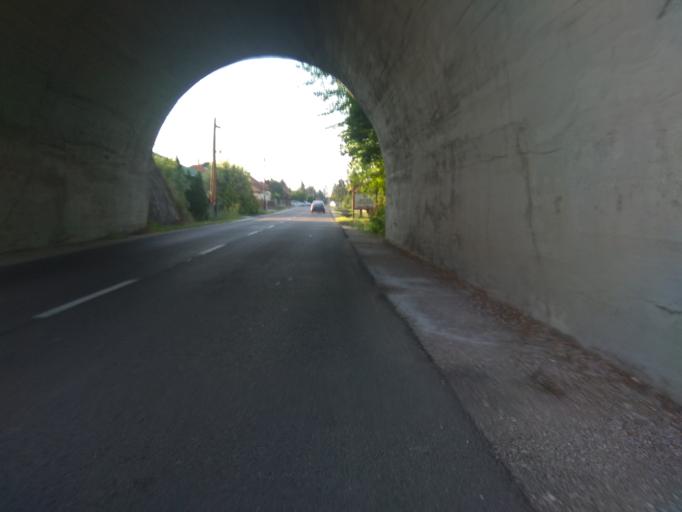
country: HU
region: Borsod-Abauj-Zemplen
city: Nyekladhaza
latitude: 47.9875
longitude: 20.8390
